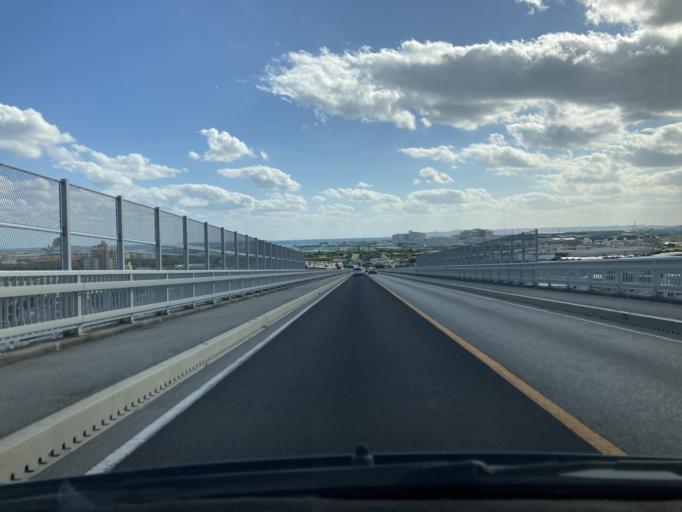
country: JP
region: Okinawa
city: Gushikawa
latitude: 26.3493
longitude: 127.8560
